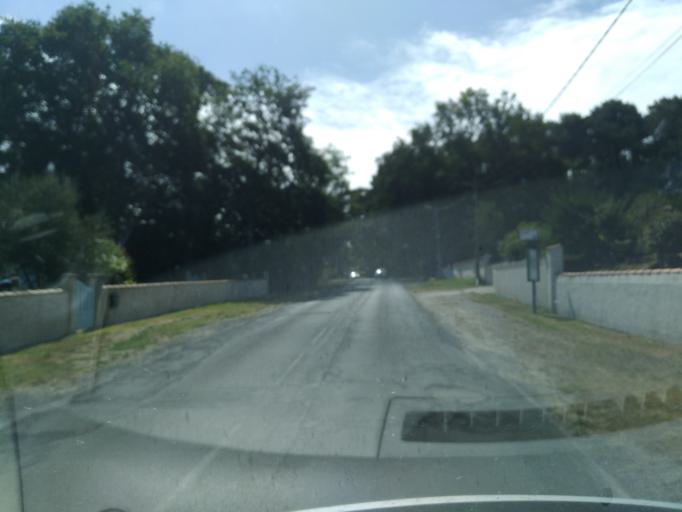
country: FR
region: Poitou-Charentes
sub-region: Departement de la Charente-Maritime
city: Saint-Palais-sur-Mer
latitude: 45.6691
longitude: -1.0834
